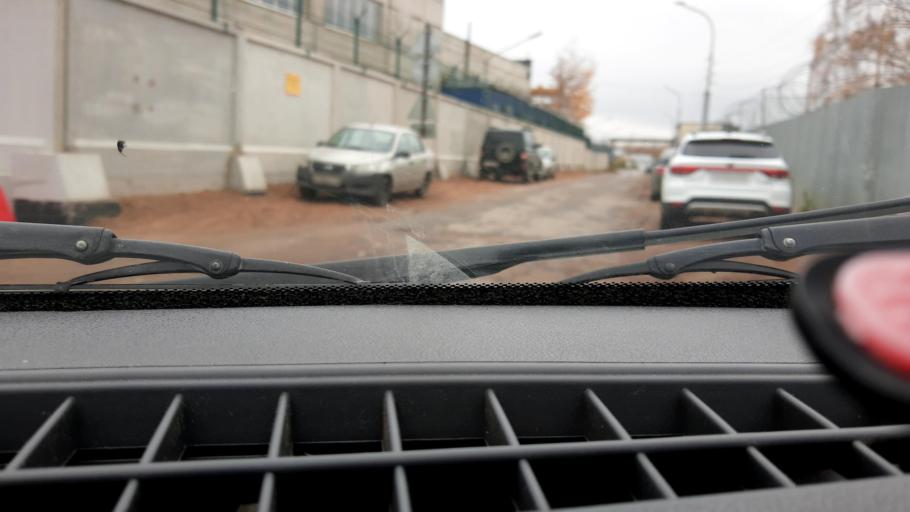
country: RU
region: Bashkortostan
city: Ufa
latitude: 54.7845
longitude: 56.0698
